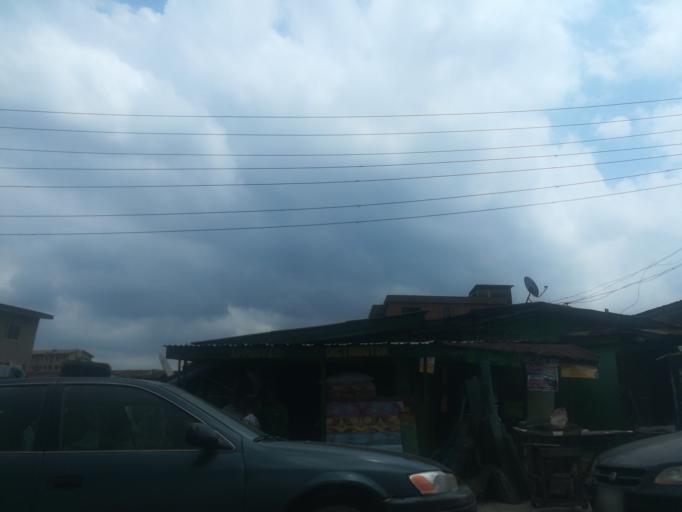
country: NG
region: Lagos
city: Ojota
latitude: 6.5976
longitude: 3.3889
